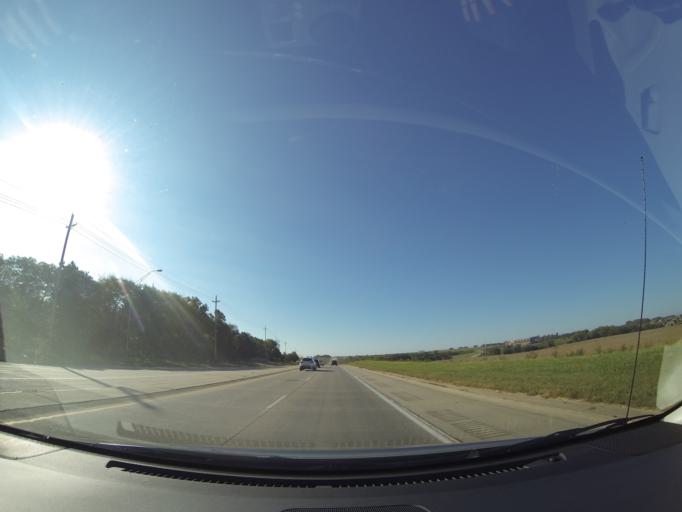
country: US
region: Nebraska
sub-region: Sarpy County
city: Gretna
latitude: 41.2044
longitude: -96.2344
